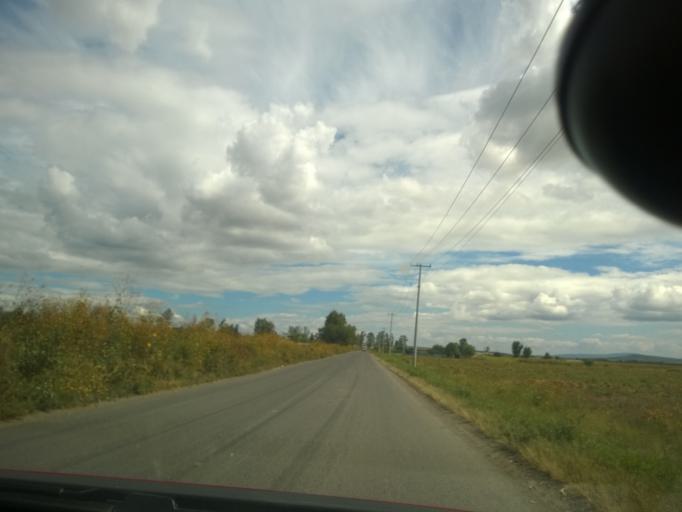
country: MX
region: Guanajuato
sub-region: Leon
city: Plan Guanajuato (La Sandia)
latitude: 20.9643
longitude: -101.6523
